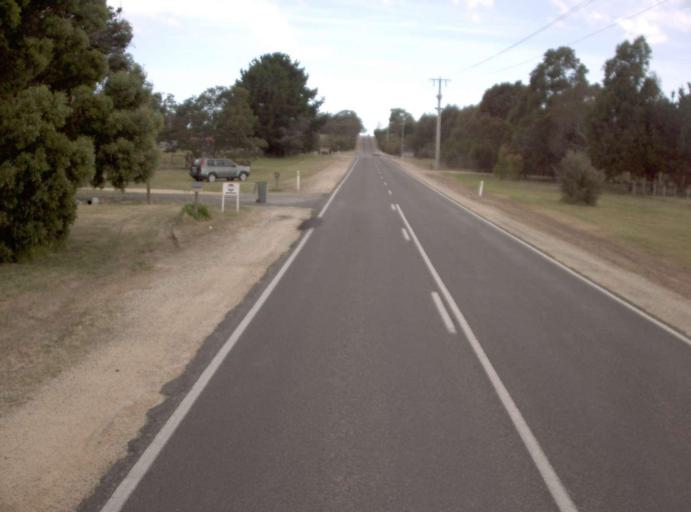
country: AU
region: Victoria
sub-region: Wellington
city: Sale
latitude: -38.1820
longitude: 147.0906
